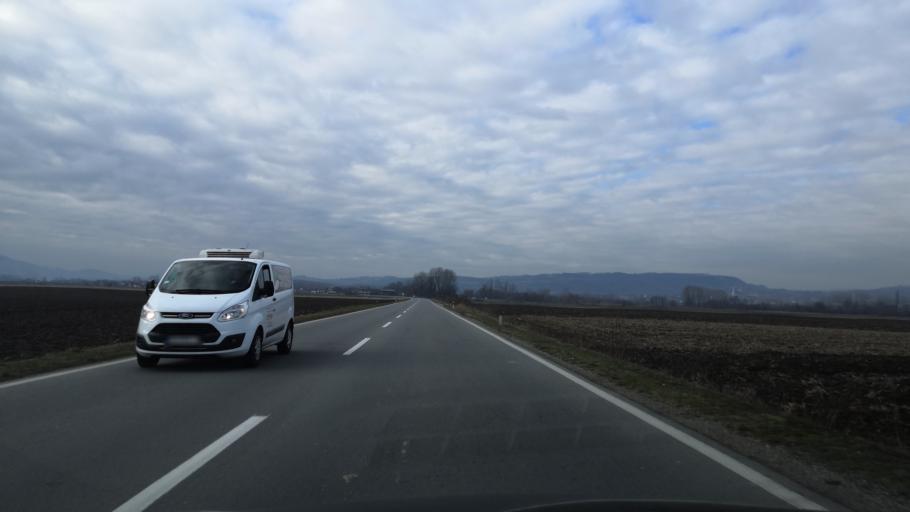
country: RS
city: Lipnicki Sor
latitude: 44.5703
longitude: 19.2119
